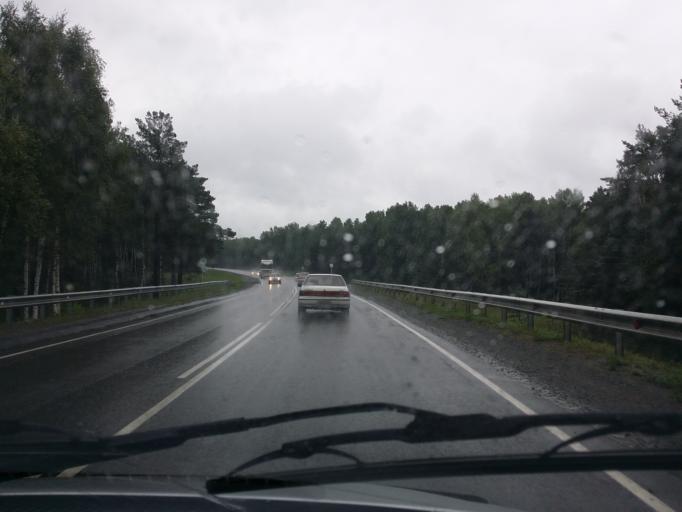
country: RU
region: Altai Krai
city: Bayunovskiye Klyuchi
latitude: 53.3417
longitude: 84.1467
